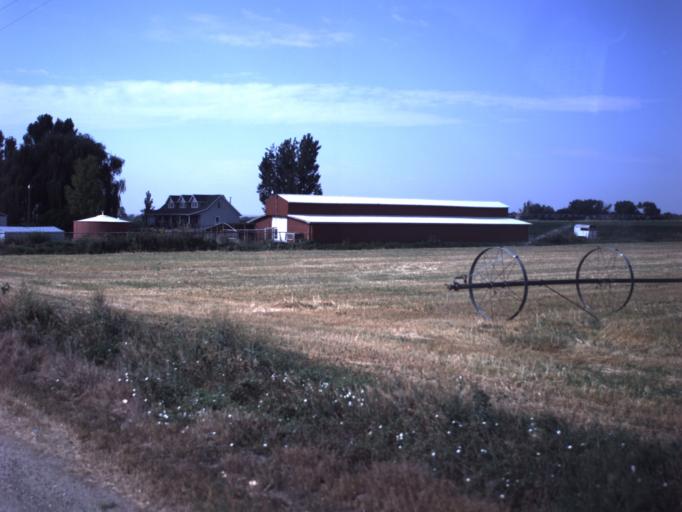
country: US
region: Utah
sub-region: Uintah County
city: Naples
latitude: 40.3838
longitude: -109.3459
